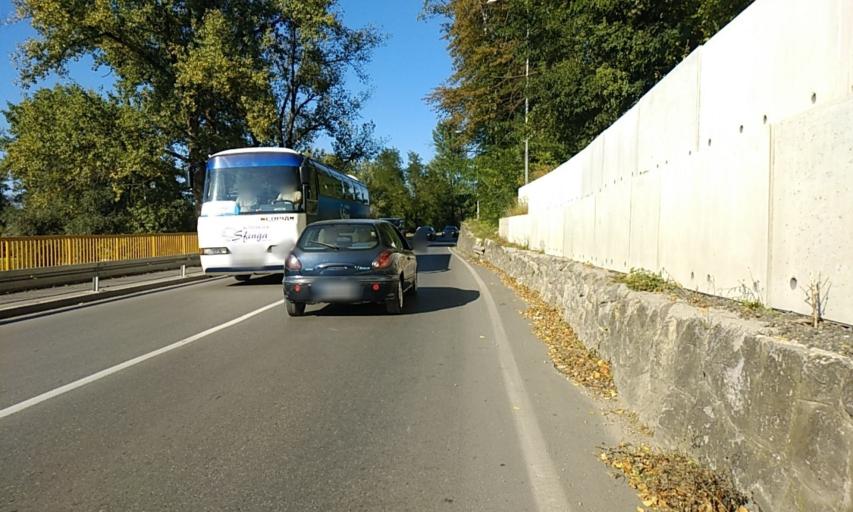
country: BA
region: Republika Srpska
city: Starcevica
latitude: 44.7673
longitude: 17.2180
